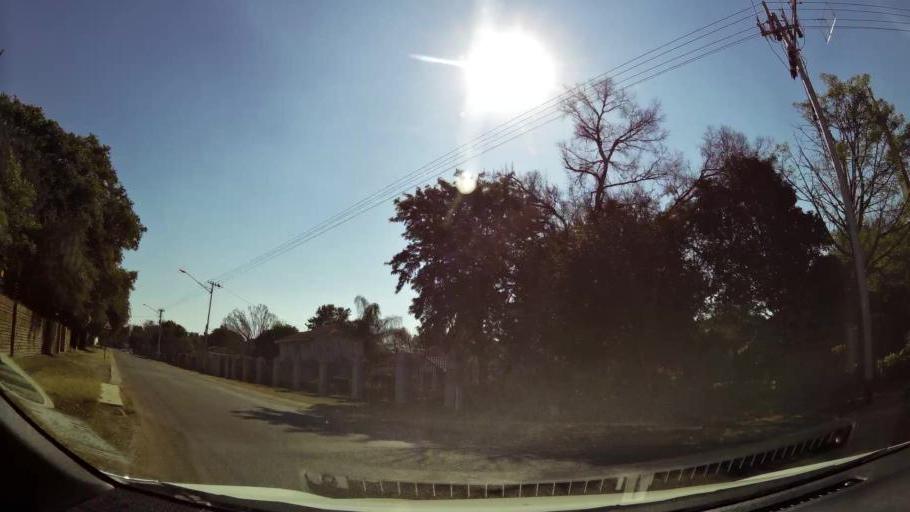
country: ZA
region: Gauteng
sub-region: City of Tshwane Metropolitan Municipality
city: Pretoria
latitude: -25.7812
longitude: 28.2664
